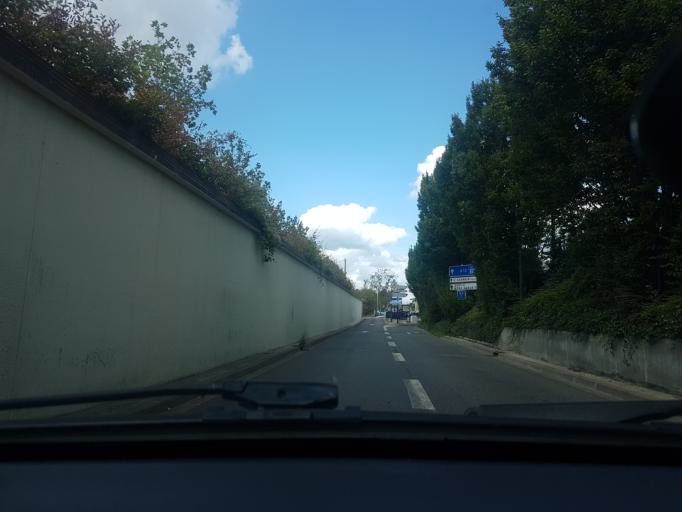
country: FR
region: Ile-de-France
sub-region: Departement des Yvelines
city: Le Chesnay
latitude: 48.8259
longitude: 2.1143
